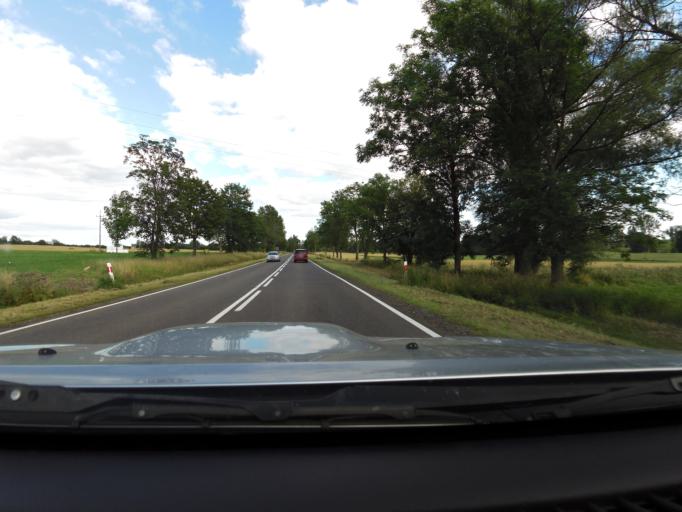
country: PL
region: Podlasie
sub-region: Powiat grajewski
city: Rajgrod
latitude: 53.8644
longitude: 22.6848
